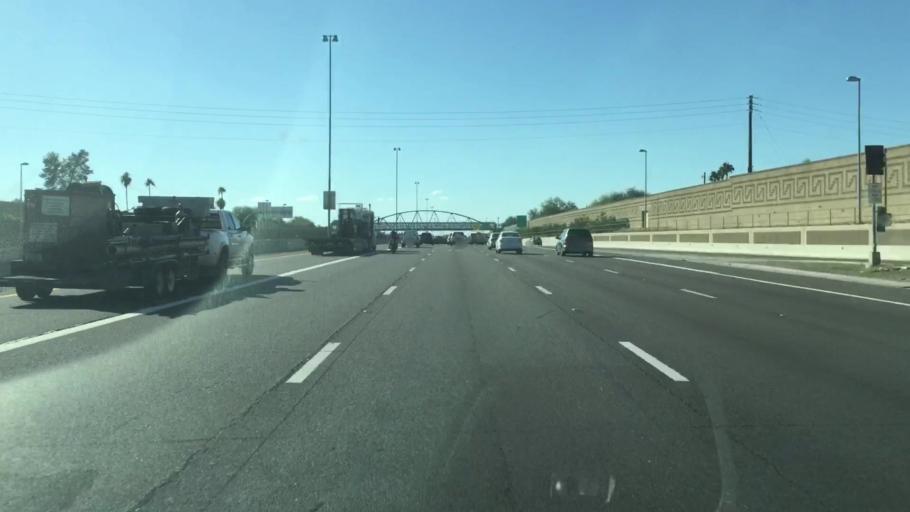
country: US
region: Arizona
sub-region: Maricopa County
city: Tempe Junction
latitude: 33.3843
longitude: -111.9307
